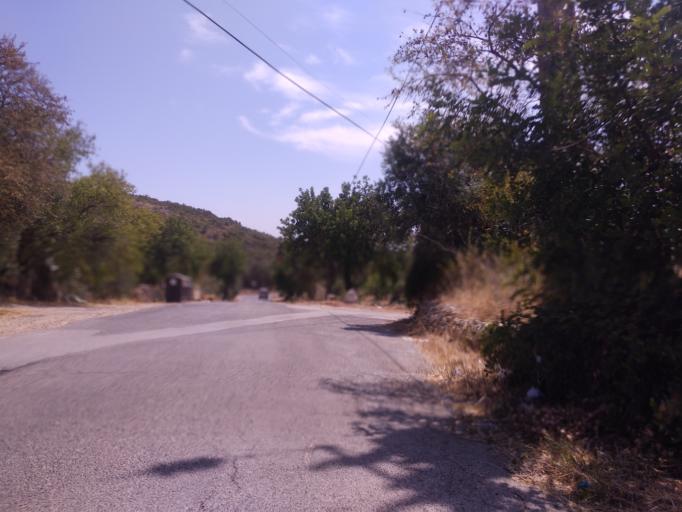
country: PT
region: Faro
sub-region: Faro
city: Santa Barbara de Nexe
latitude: 37.1112
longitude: -7.9468
